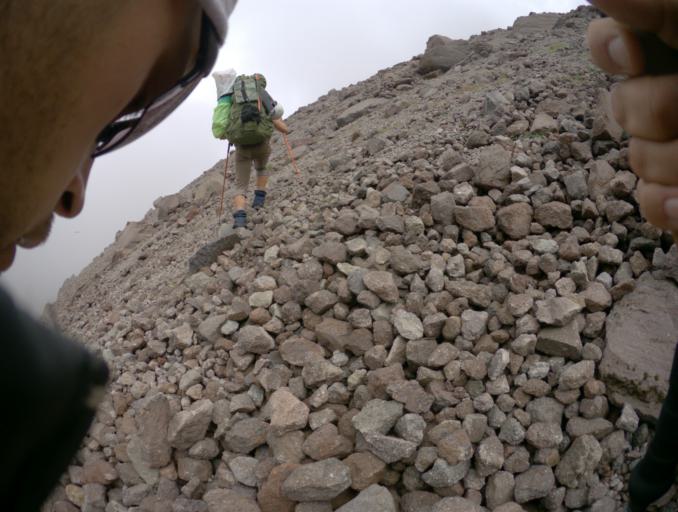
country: RU
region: Kabardino-Balkariya
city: Terskol
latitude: 43.3836
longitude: 42.3732
